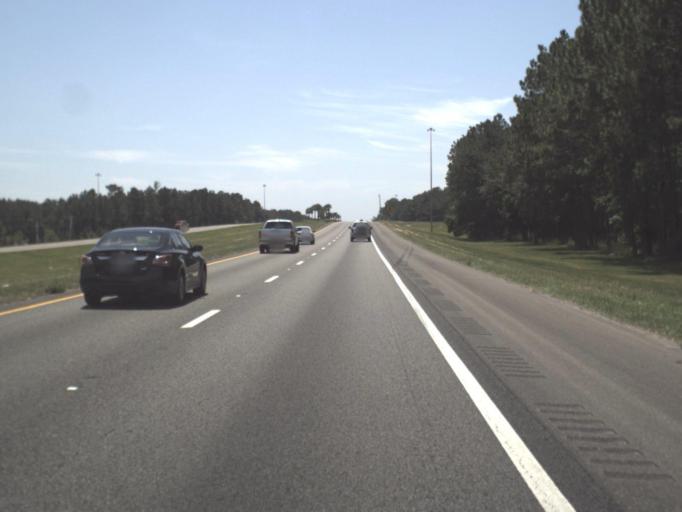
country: US
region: Florida
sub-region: Nassau County
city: Nassau Village-Ratliff
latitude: 30.4417
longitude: -81.7225
